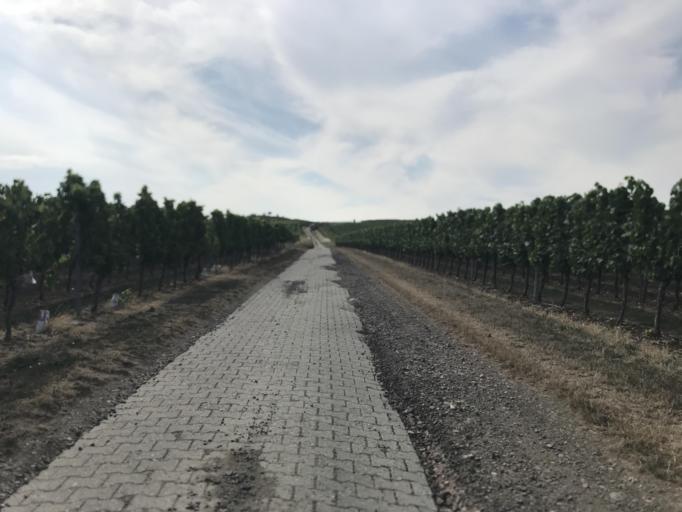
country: DE
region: Rheinland-Pfalz
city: Bechtolsheim
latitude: 49.8013
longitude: 8.1981
